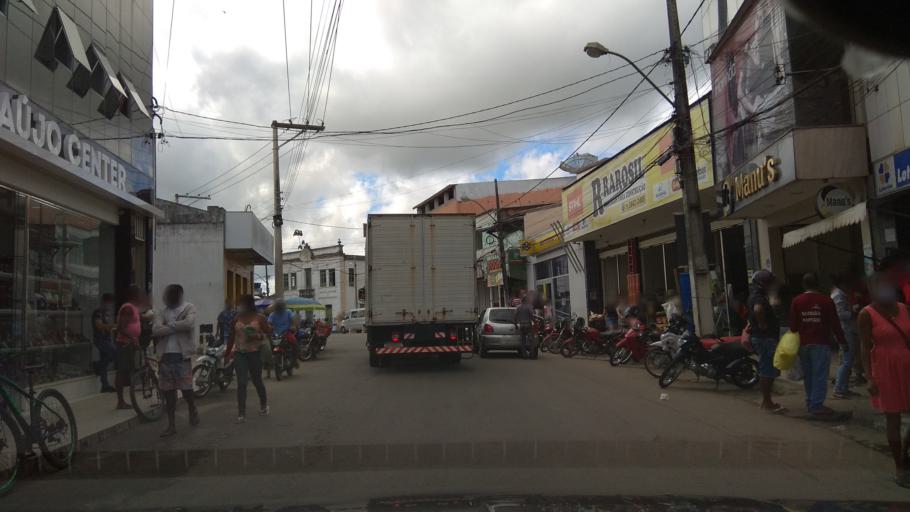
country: BR
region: Bahia
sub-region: Mutuipe
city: Mutuipe
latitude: -13.1833
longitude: -39.4231
